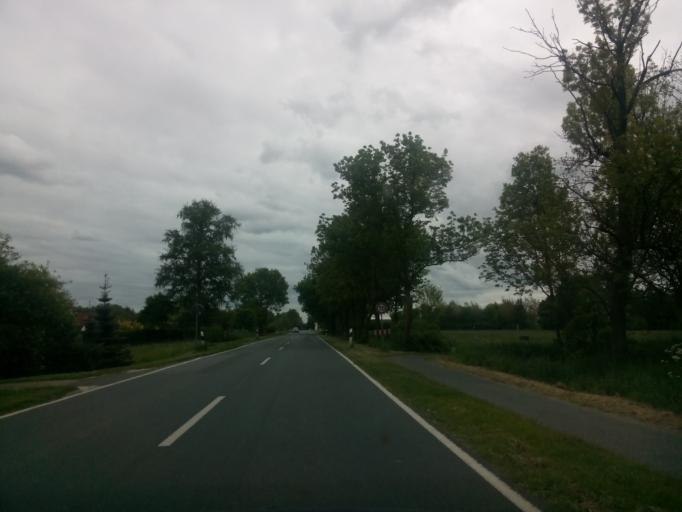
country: DE
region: Lower Saxony
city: Lemwerder
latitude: 53.1286
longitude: 8.6268
